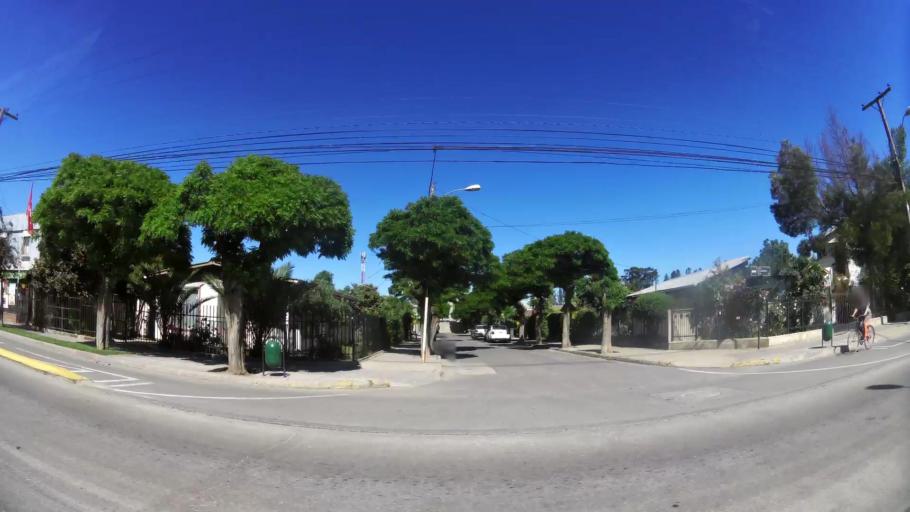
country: CL
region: Valparaiso
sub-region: Provincia de Marga Marga
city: Quilpue
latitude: -33.3122
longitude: -71.4092
